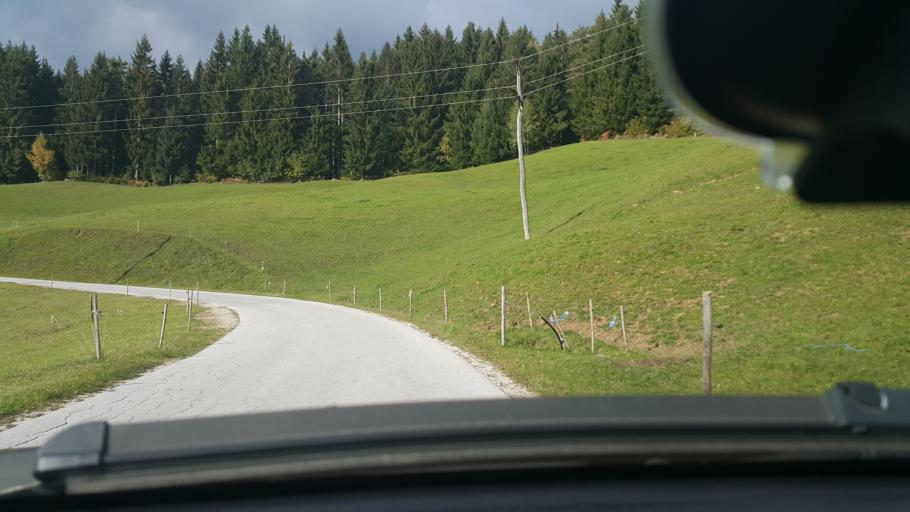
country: SI
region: Vitanje
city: Vitanje
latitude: 46.4094
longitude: 15.2841
